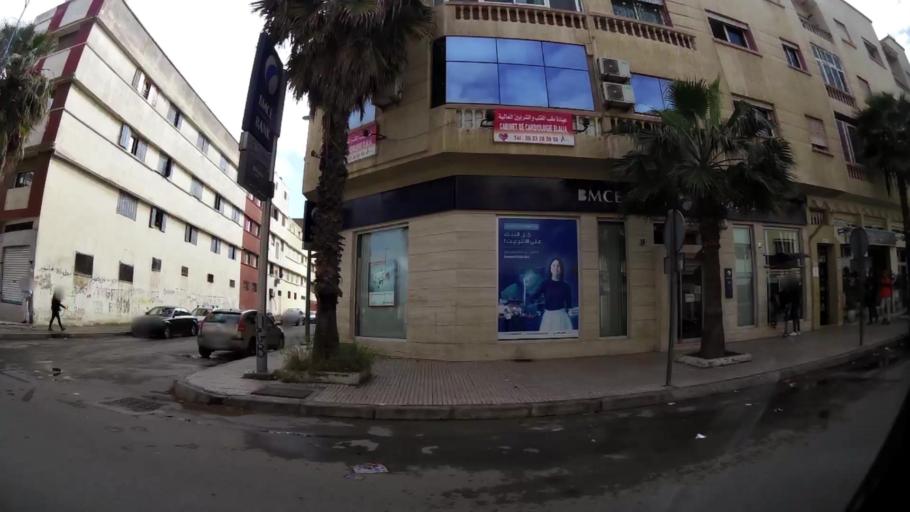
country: MA
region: Grand Casablanca
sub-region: Mohammedia
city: Mohammedia
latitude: 33.6926
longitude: -7.3854
